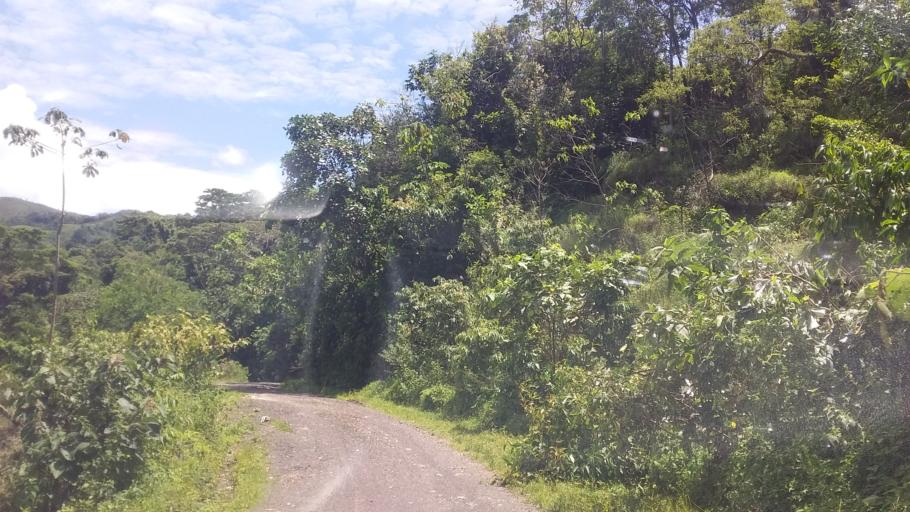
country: CO
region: Casanare
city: Nunchia
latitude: 5.6274
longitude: -72.3341
